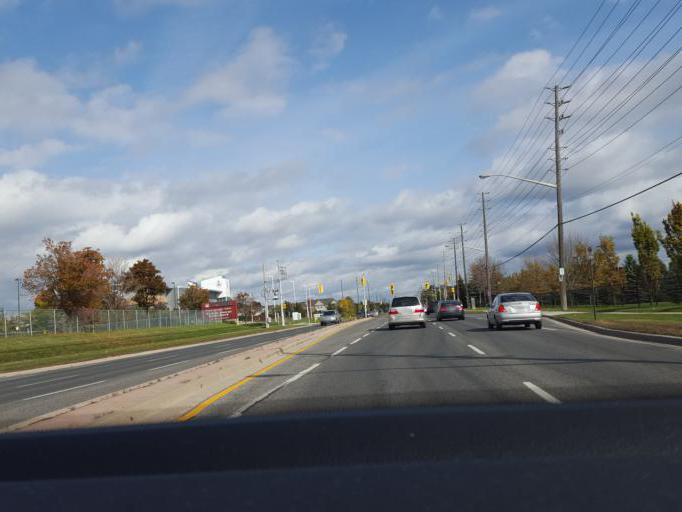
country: CA
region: Ontario
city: Oshawa
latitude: 43.9188
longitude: -78.9415
